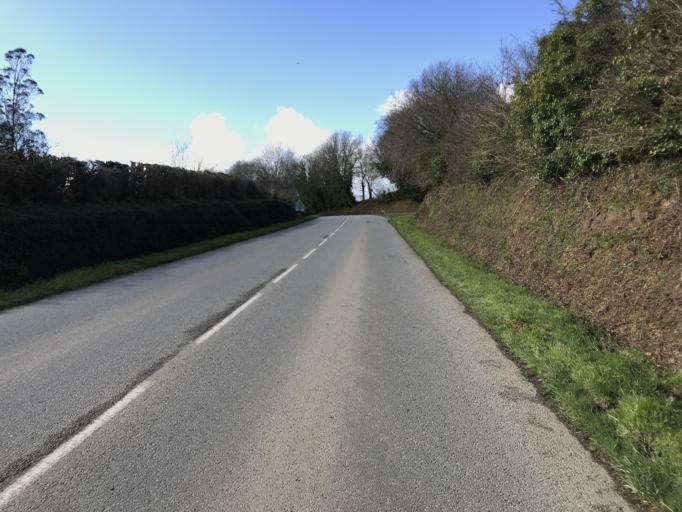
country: FR
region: Brittany
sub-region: Departement du Finistere
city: Loperhet
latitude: 48.3810
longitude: -4.3305
